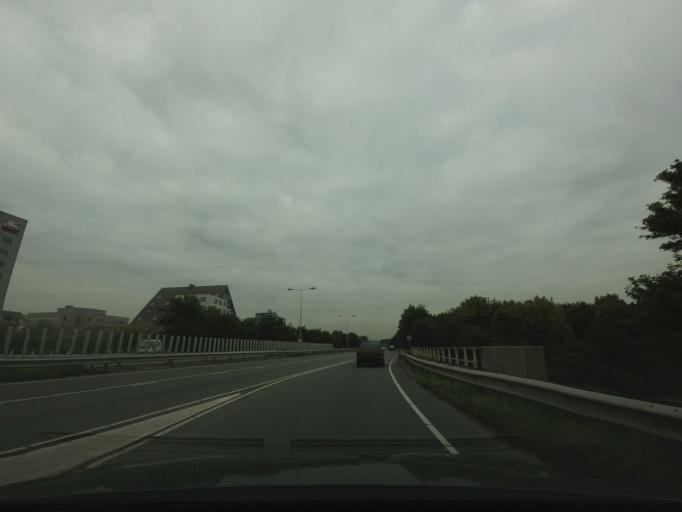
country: NL
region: North Holland
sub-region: Gemeente Diemen
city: Diemen
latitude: 52.3256
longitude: 4.9556
